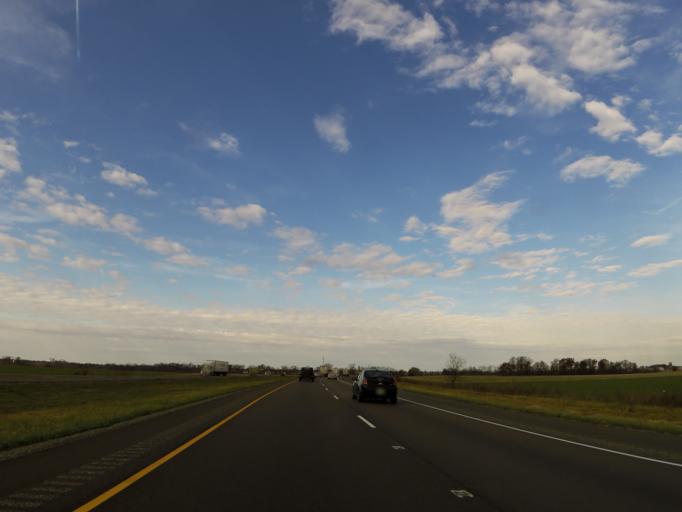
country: US
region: Illinois
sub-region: Washington County
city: Okawville
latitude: 38.4319
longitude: -89.5124
